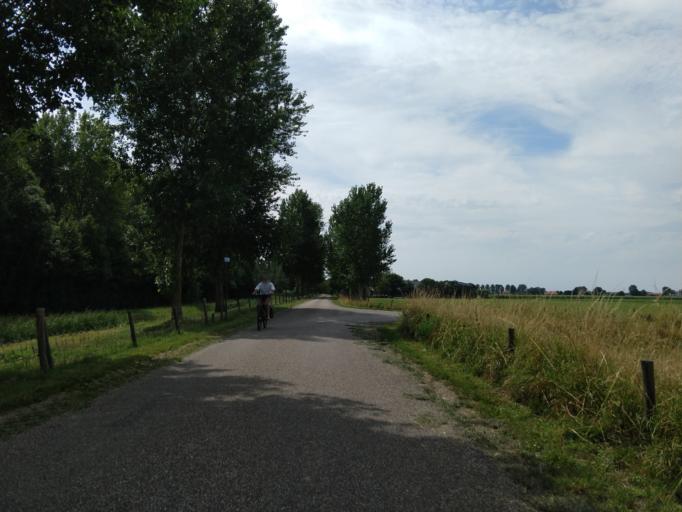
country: NL
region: Zeeland
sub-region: Gemeente Middelburg
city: Middelburg
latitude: 51.4738
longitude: 3.6742
